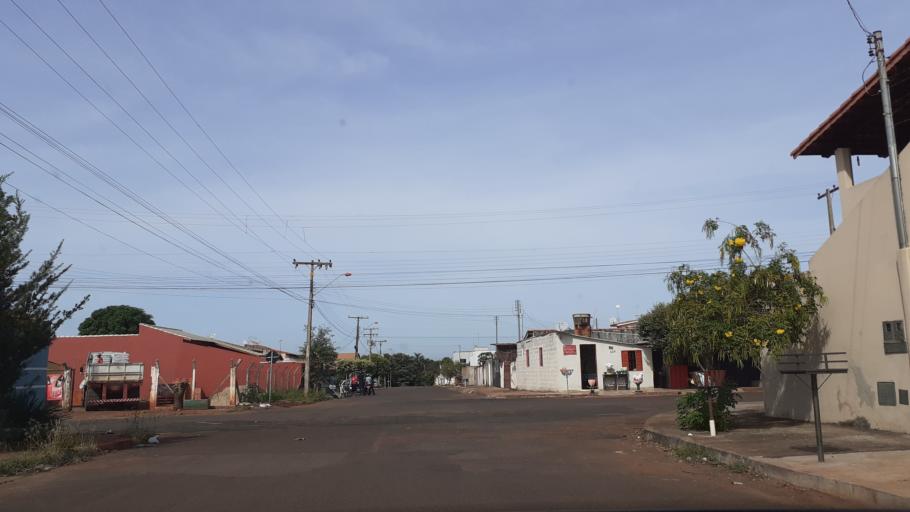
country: BR
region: Goias
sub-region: Itumbiara
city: Itumbiara
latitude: -18.4226
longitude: -49.2420
